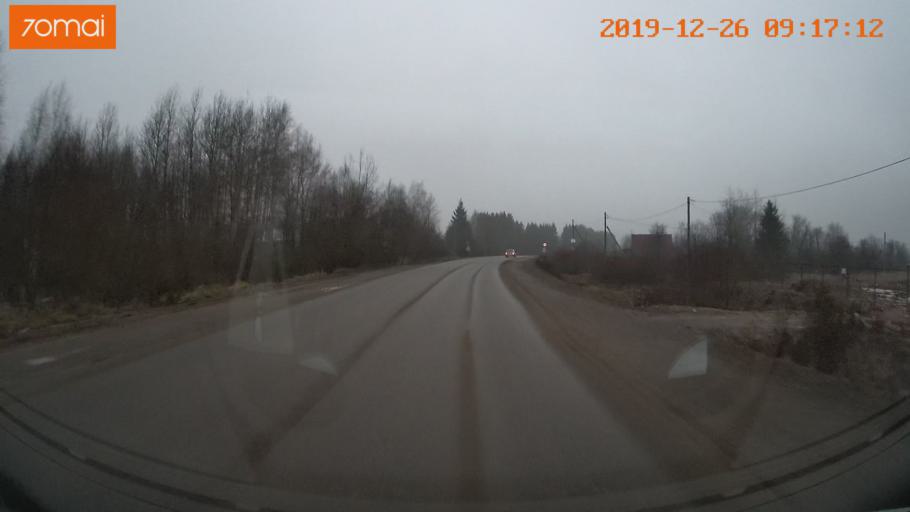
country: RU
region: Vologda
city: Gryazovets
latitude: 58.9270
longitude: 40.2386
